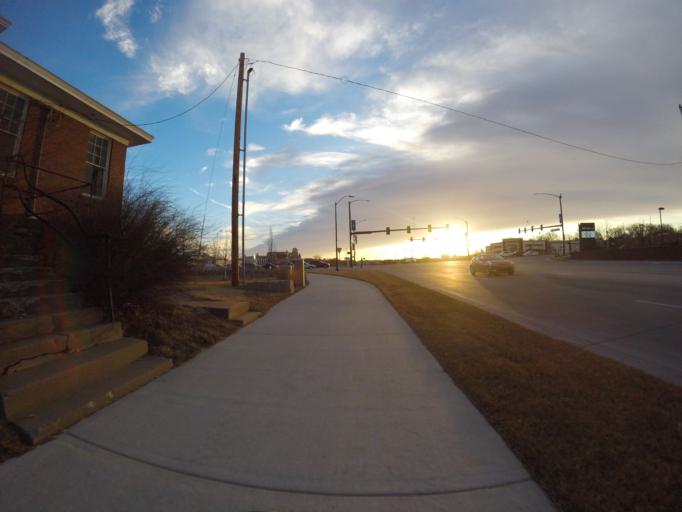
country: US
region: Kansas
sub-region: Douglas County
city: Lawrence
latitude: 38.9427
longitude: -95.2654
